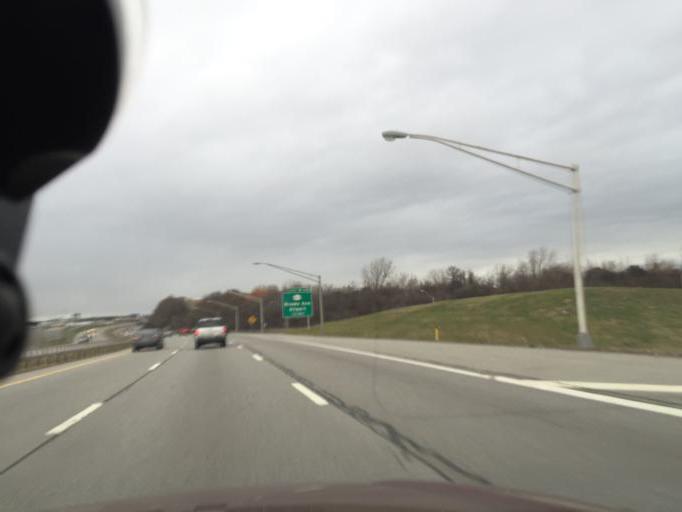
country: US
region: New York
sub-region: Monroe County
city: Rochester
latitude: 43.1236
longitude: -77.6497
